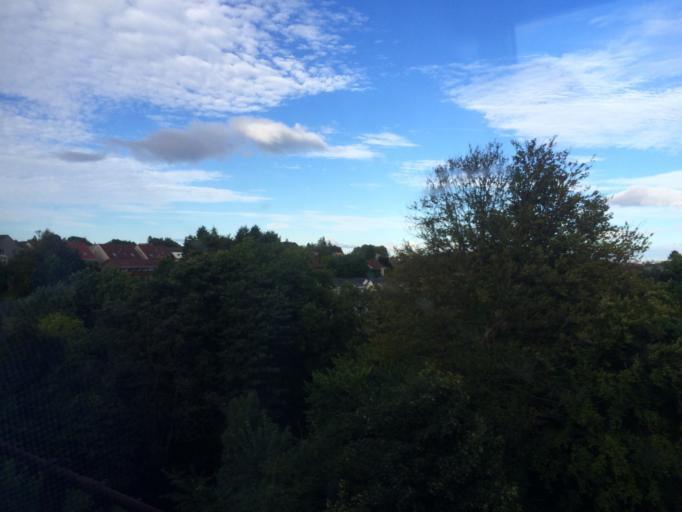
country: GB
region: Scotland
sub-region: Falkirk
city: Larbert
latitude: 56.0162
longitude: -3.8321
